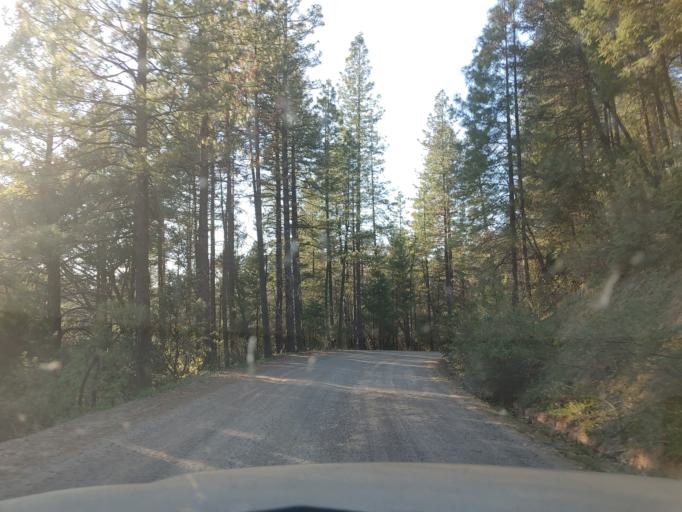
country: US
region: California
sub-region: Shasta County
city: Bella Vista
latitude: 40.8106
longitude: -122.0033
